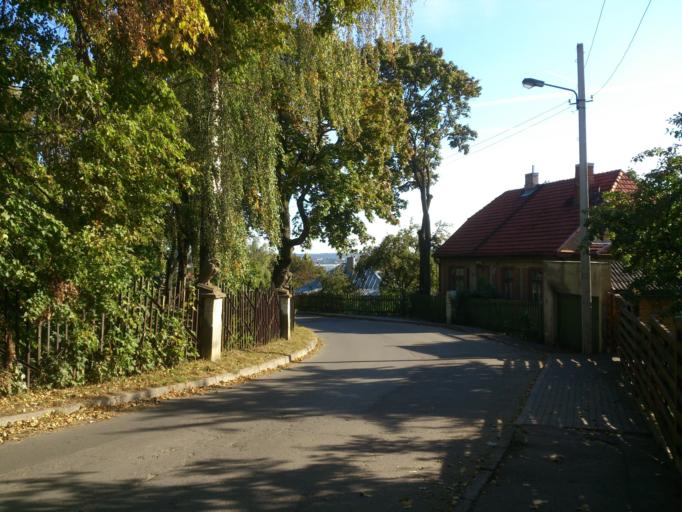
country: LT
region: Kauno apskritis
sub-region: Kaunas
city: Kaunas
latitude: 54.9002
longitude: 23.8991
